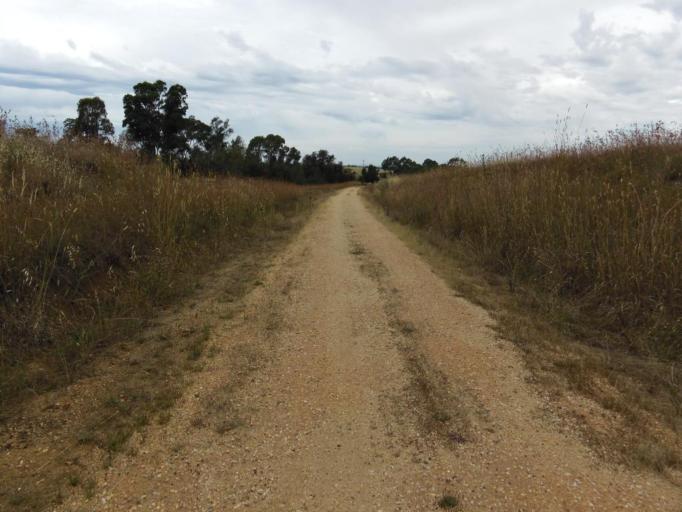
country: AU
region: Victoria
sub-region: Greater Bendigo
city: Kennington
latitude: -36.8596
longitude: 144.6225
